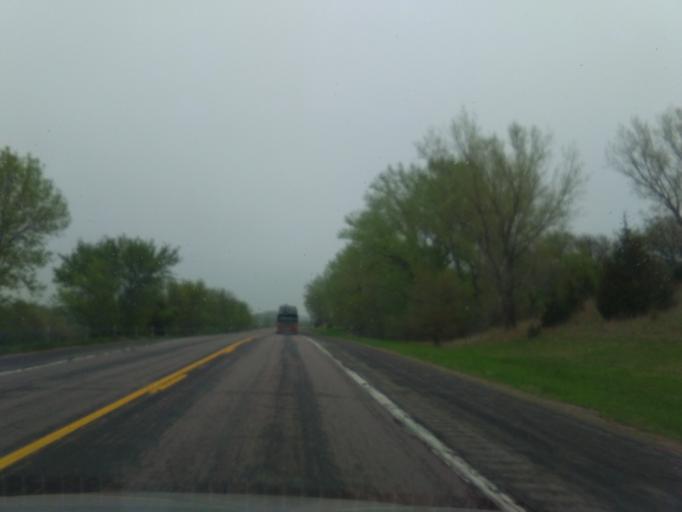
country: US
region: Nebraska
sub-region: Burt County
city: Oakland
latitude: 41.7978
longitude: -96.4830
